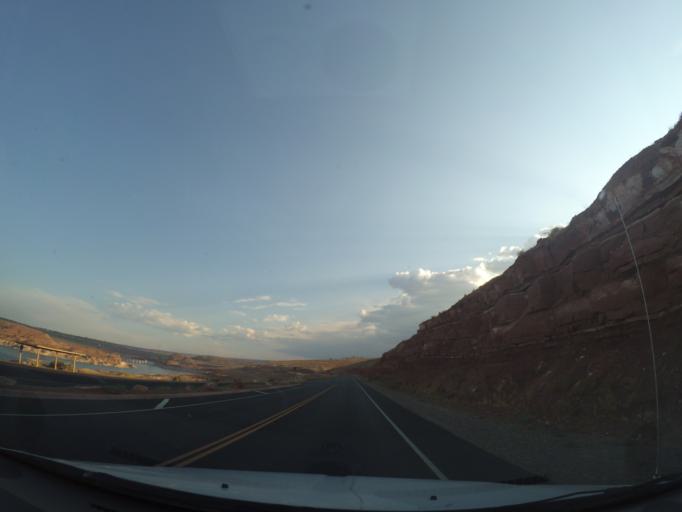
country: US
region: Arizona
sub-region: Coconino County
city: Page
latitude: 36.9640
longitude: -111.4916
